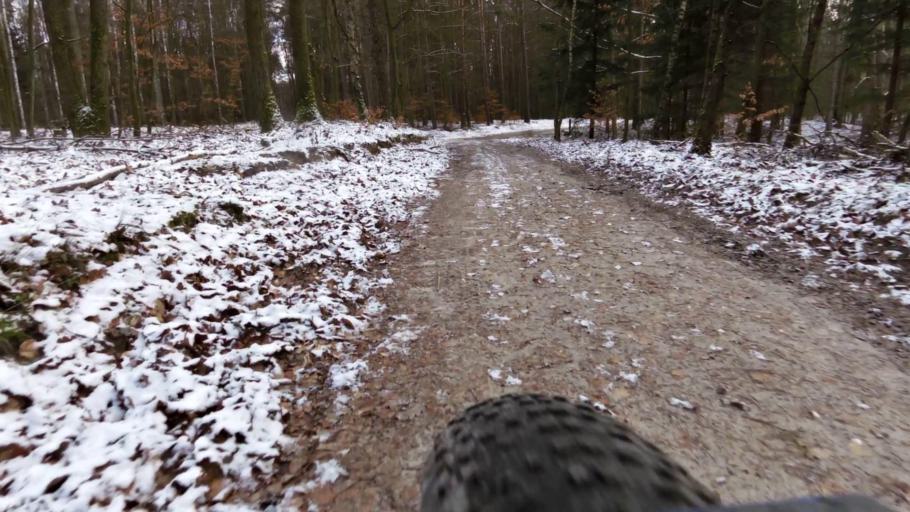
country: PL
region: West Pomeranian Voivodeship
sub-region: Powiat walecki
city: Walcz
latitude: 53.2773
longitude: 16.3078
